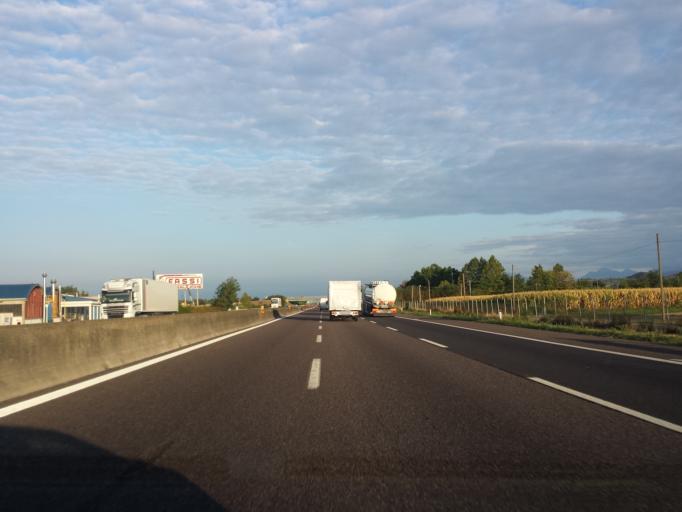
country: IT
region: Lombardy
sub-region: Provincia di Bergamo
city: Bolgare
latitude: 45.6398
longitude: 9.8247
